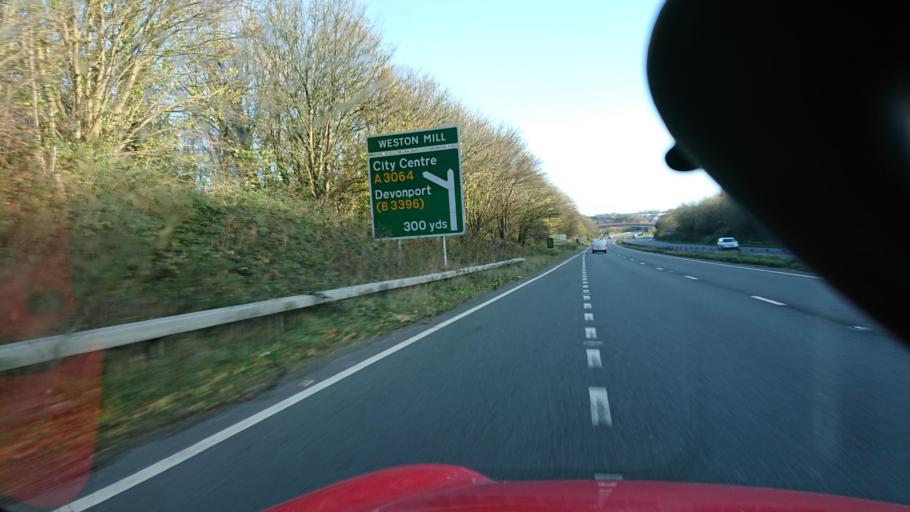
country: GB
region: England
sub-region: Cornwall
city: Torpoint
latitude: 50.4104
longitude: -4.1712
